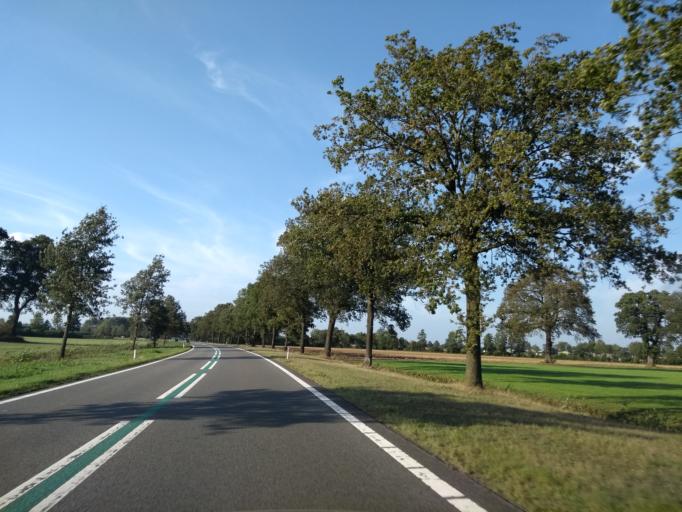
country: NL
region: Overijssel
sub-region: Gemeente Almelo
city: Almelo
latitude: 52.3869
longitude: 6.6661
